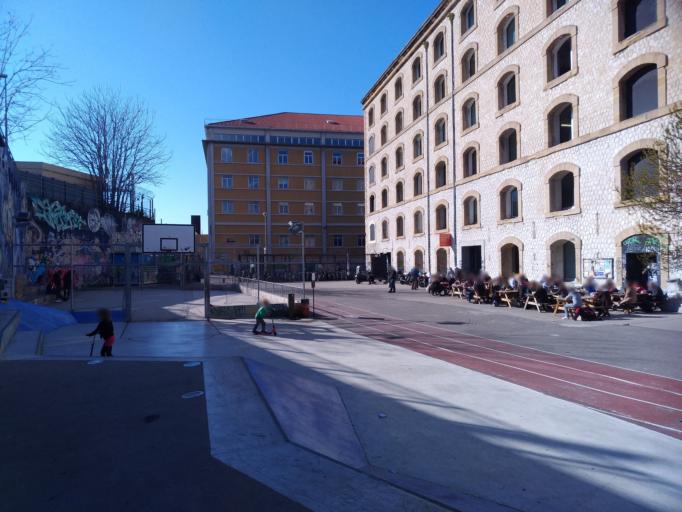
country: FR
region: Provence-Alpes-Cote d'Azur
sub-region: Departement des Bouches-du-Rhone
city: Marseille 04
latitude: 43.3099
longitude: 5.3910
